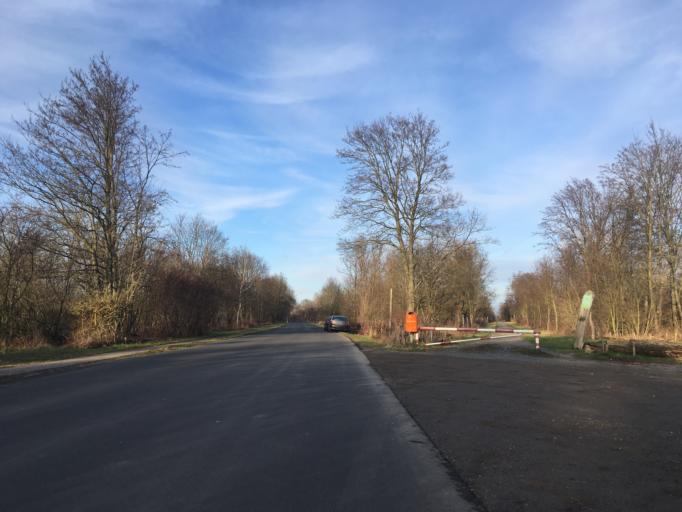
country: DE
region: Berlin
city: Blankenfelde
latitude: 52.6275
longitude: 13.4002
